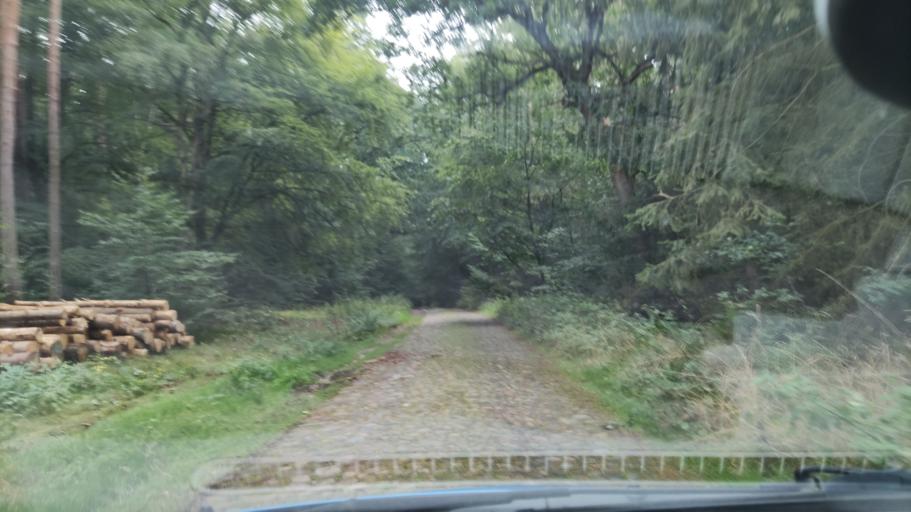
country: DE
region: Lower Saxony
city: Altenmedingen
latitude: 53.1511
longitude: 10.5812
